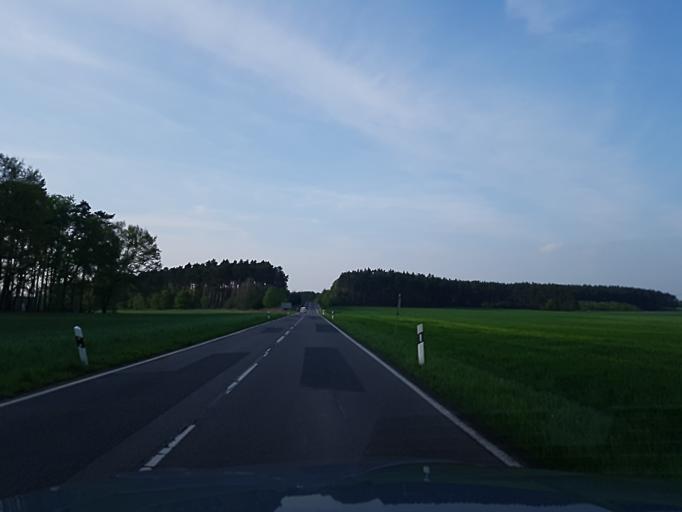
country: DE
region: Brandenburg
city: Bad Liebenwerda
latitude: 51.5267
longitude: 13.4115
